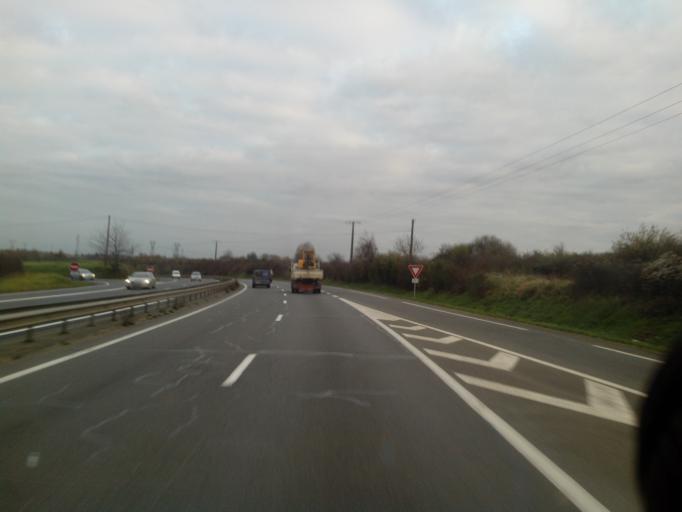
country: FR
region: Poitou-Charentes
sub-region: Departement de la Vienne
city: Chasseneuil-du-Poitou
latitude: 46.6140
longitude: 0.3680
